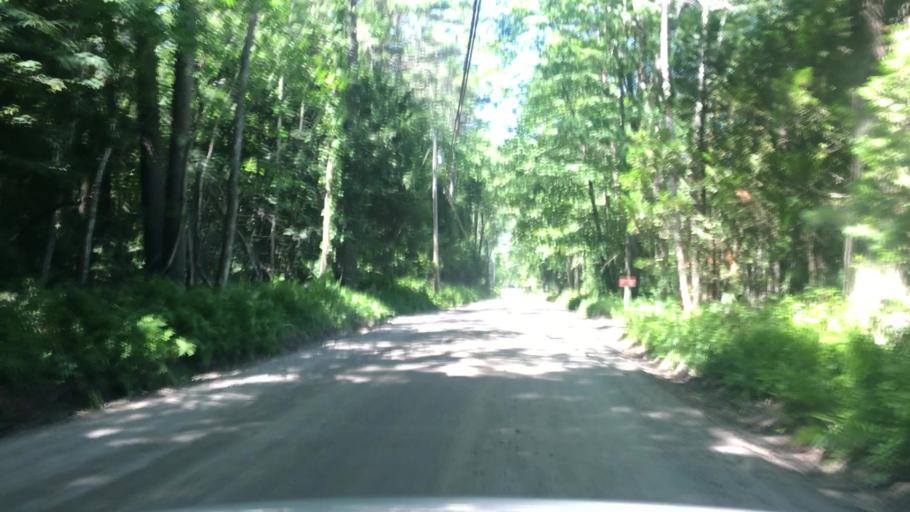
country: US
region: New Hampshire
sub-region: Merrimack County
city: Hopkinton
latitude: 43.2289
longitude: -71.6689
